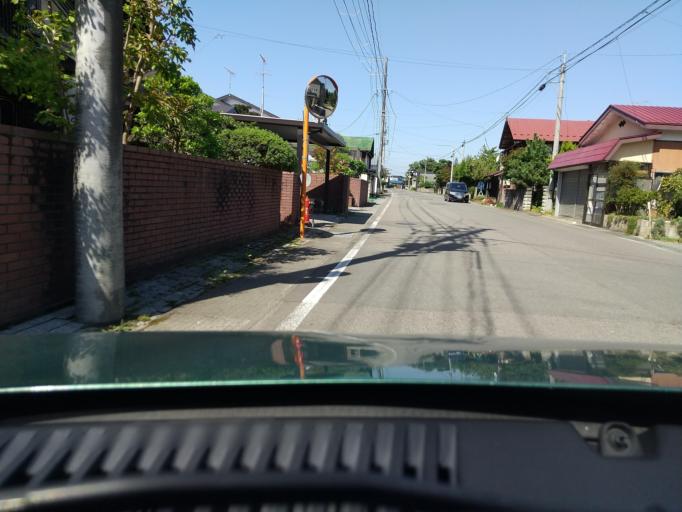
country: JP
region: Akita
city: Omagari
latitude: 39.6106
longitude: 140.3236
